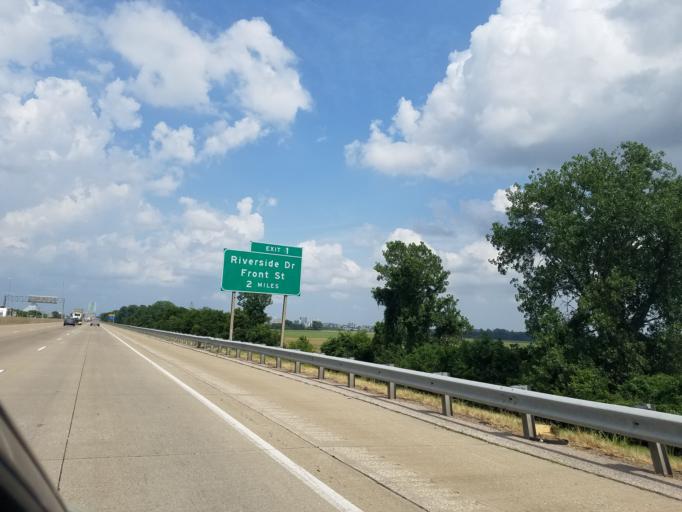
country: US
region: Tennessee
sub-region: Shelby County
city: Memphis
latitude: 35.1320
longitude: -90.0792
